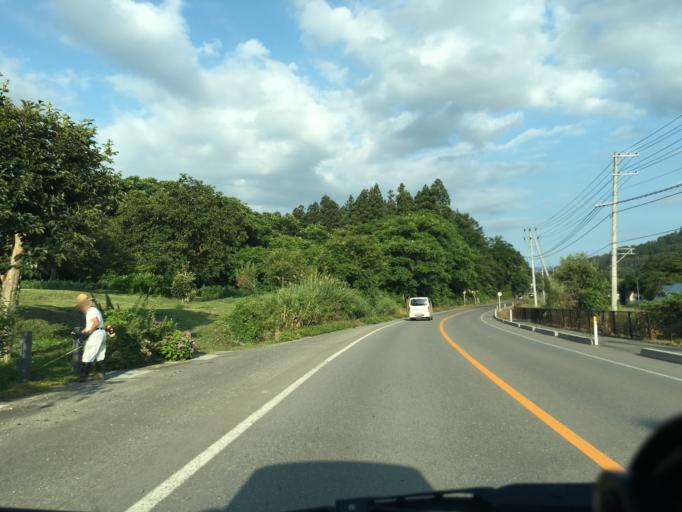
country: JP
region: Yamagata
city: Yonezawa
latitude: 37.9152
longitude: 140.0614
